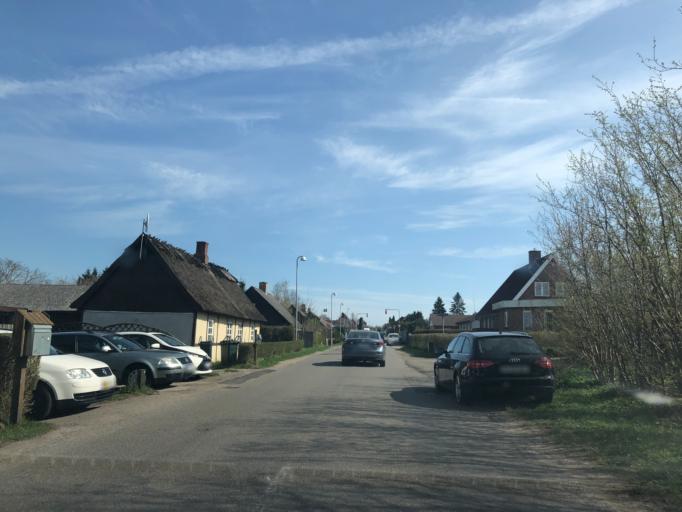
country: DK
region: Zealand
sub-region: Faxe Kommune
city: Fakse
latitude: 55.2683
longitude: 12.1061
